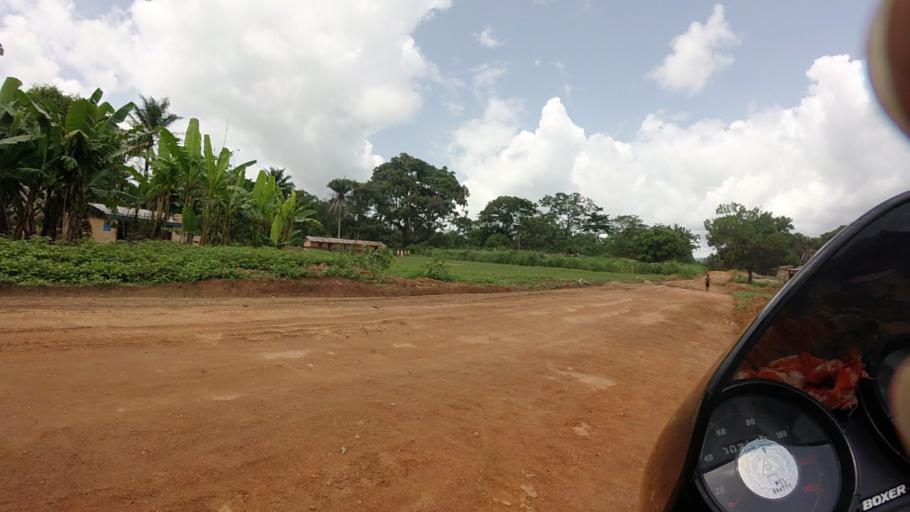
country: SL
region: Eastern Province
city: Koidu
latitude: 8.6342
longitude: -10.8458
